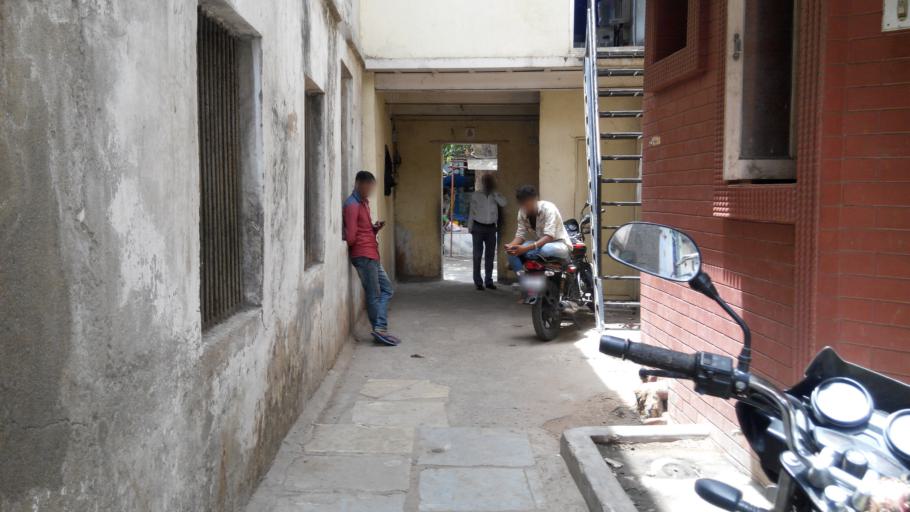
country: IN
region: Gujarat
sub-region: Ahmadabad
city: Ahmedabad
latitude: 23.0363
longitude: 72.5918
